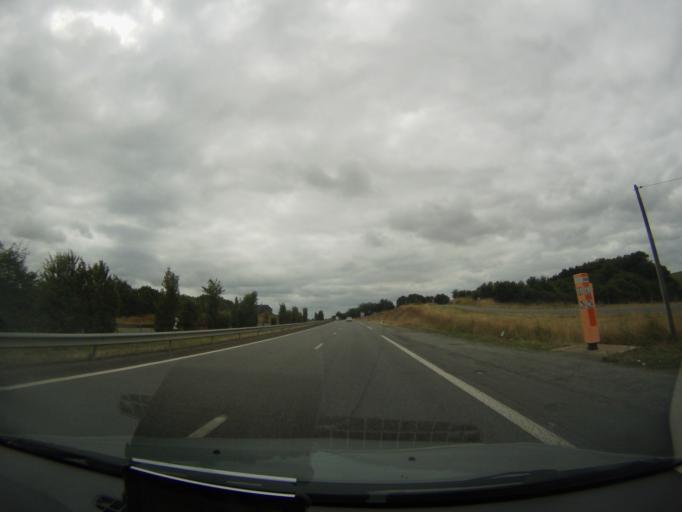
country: FR
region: Brittany
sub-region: Departement d'Ille-et-Vilaine
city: Crevin
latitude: 47.9160
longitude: -1.6813
